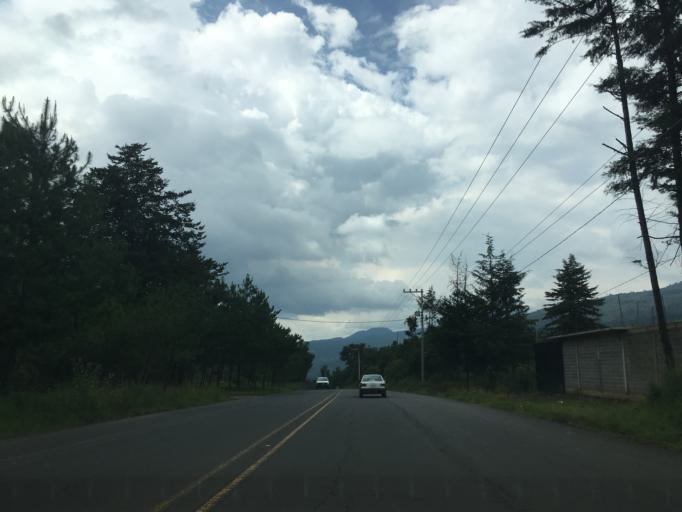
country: MX
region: Michoacan
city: Capacuaro
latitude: 19.5319
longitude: -102.0838
